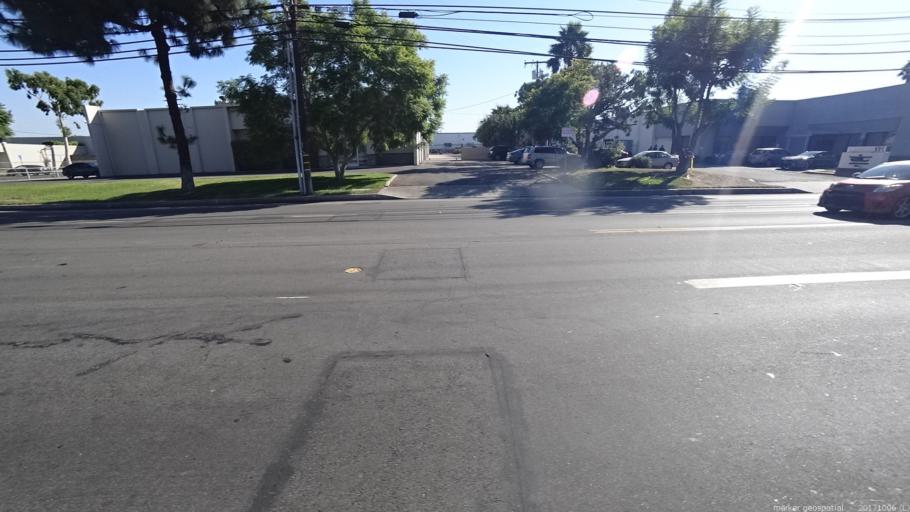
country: US
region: California
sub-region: Orange County
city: Westminster
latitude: 33.7811
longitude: -118.0098
